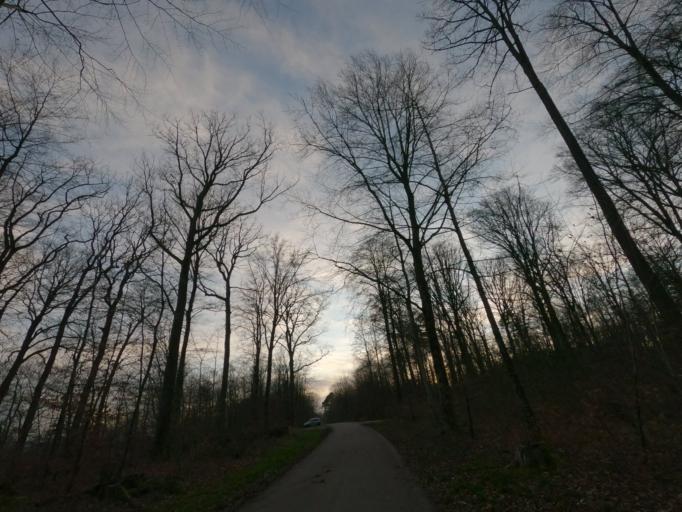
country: DE
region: Baden-Wuerttemberg
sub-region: Regierungsbezirk Stuttgart
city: Eislingen
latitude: 48.7170
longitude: 9.6829
